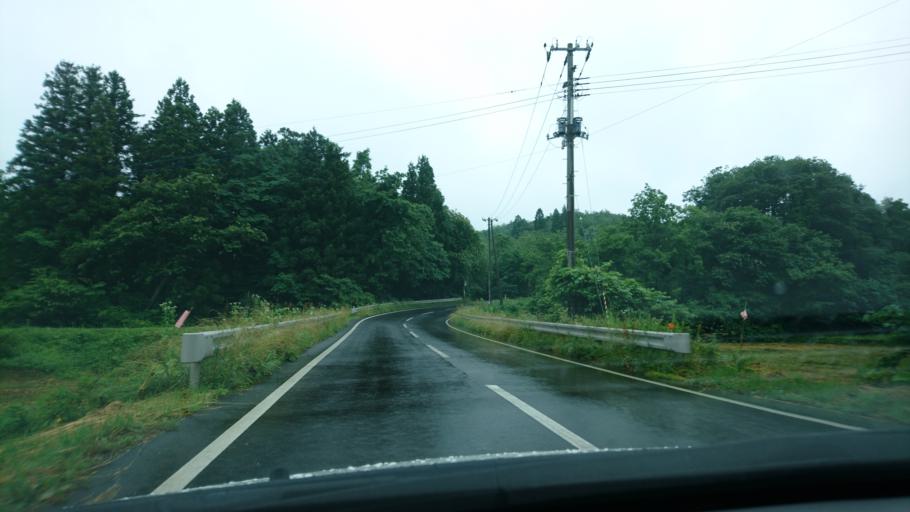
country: JP
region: Iwate
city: Ichinoseki
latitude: 38.9204
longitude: 141.0265
